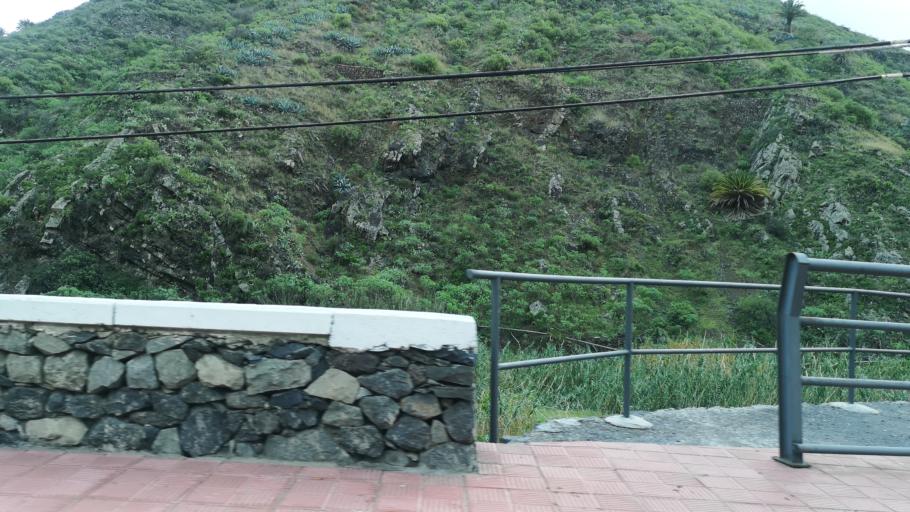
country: ES
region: Canary Islands
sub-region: Provincia de Santa Cruz de Tenerife
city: Hermigua
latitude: 28.1656
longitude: -17.1971
